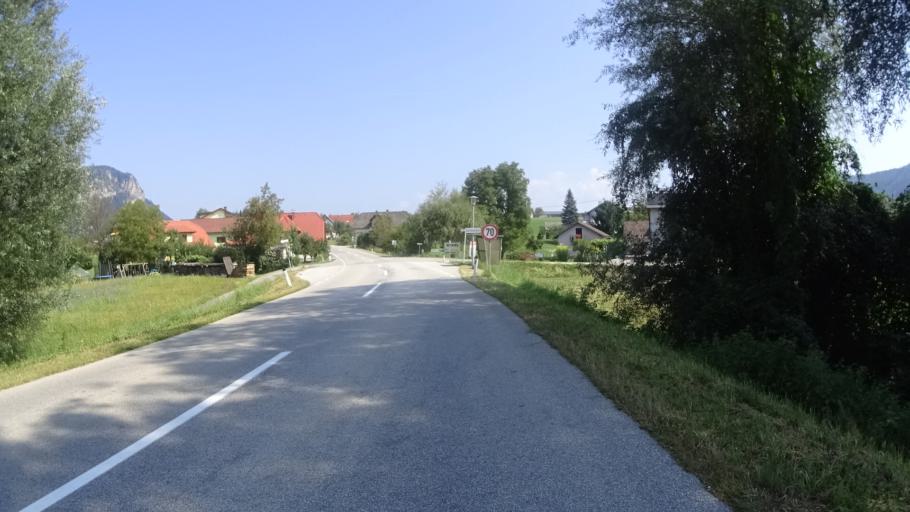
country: AT
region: Carinthia
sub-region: Politischer Bezirk Volkermarkt
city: Gallizien
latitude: 46.5706
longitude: 14.5074
